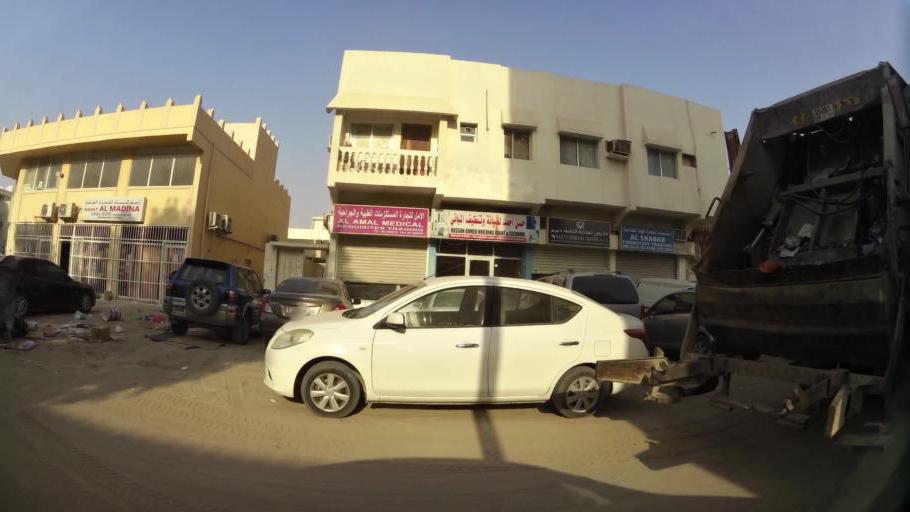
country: AE
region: Ajman
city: Ajman
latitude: 25.3846
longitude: 55.4474
